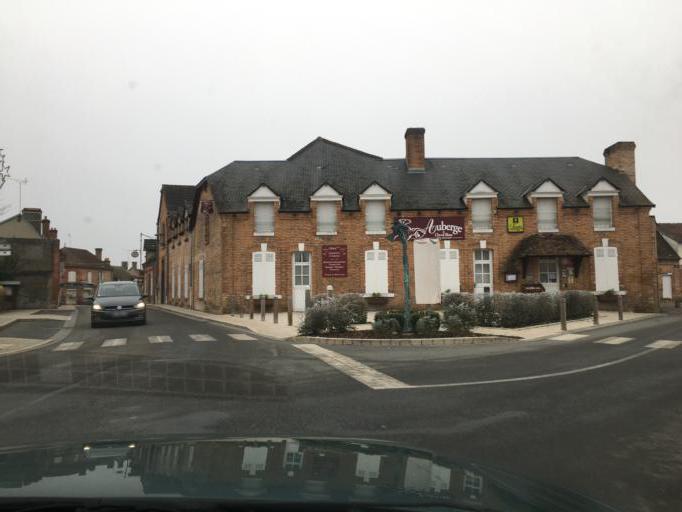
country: FR
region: Centre
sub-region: Departement du Loir-et-Cher
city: Chaumont-sur-Tharonne
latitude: 47.6327
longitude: 1.8531
